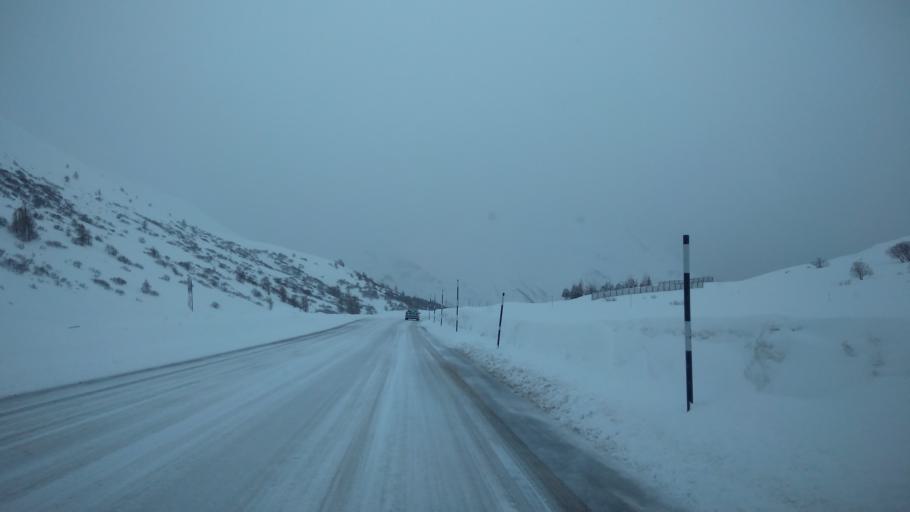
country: FR
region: Provence-Alpes-Cote d'Azur
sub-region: Departement des Hautes-Alpes
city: Le Monetier-les-Bains
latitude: 45.0335
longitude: 6.3985
